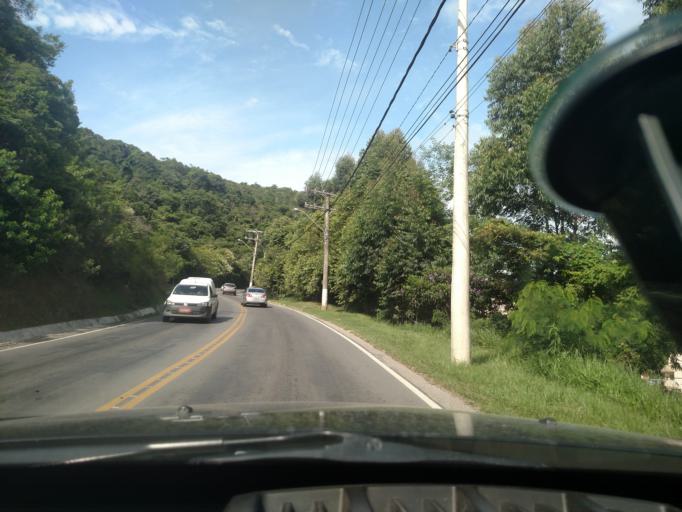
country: BR
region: Santa Catarina
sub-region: Porto Belo
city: Porto Belo
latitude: -27.1364
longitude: -48.5156
